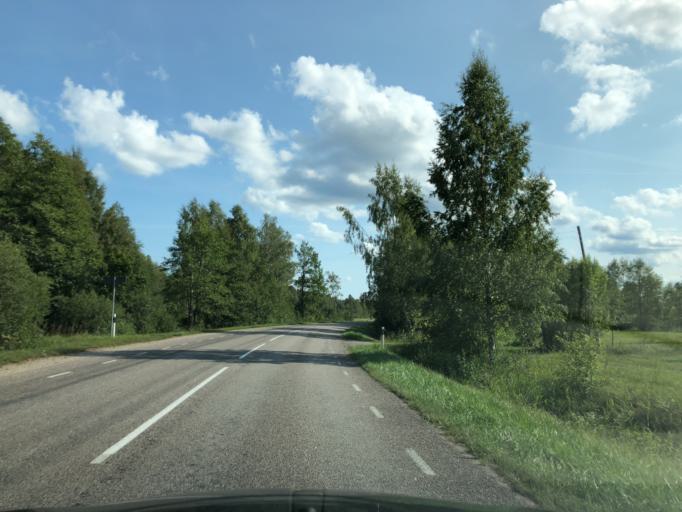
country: EE
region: Hiiumaa
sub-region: Kaerdla linn
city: Kardla
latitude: 58.7242
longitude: 22.5612
